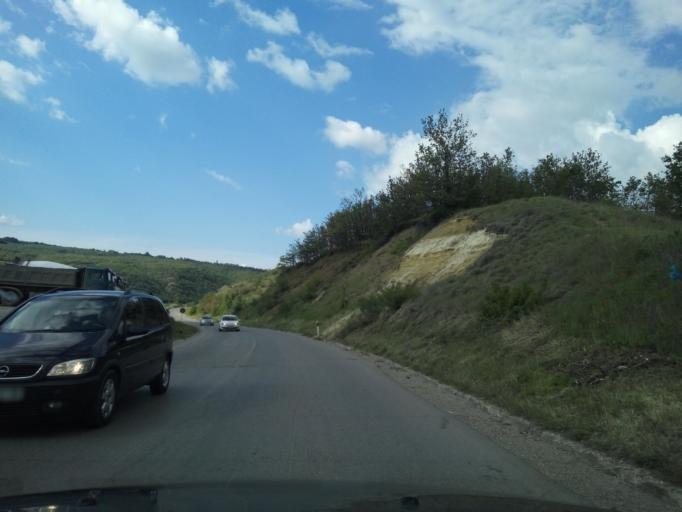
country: XK
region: Pec
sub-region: Komuna e Pejes
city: Kosuriq
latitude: 42.4962
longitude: 20.5210
